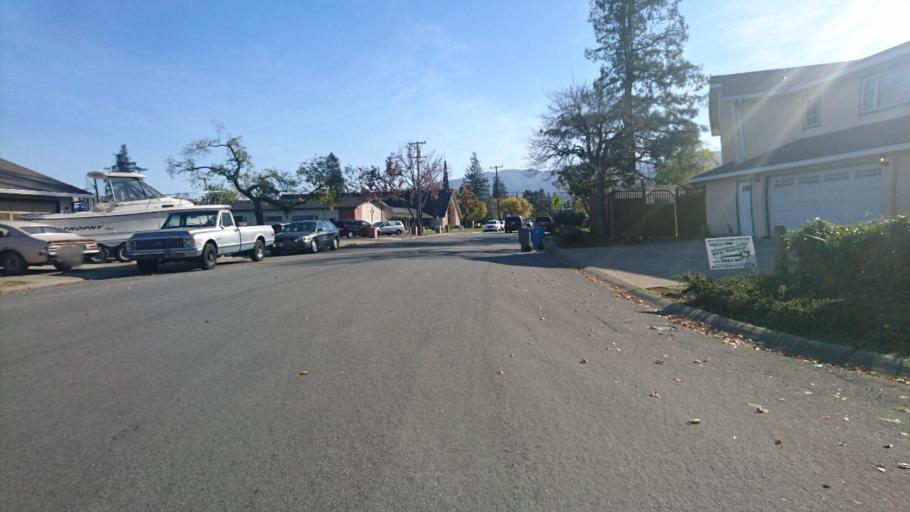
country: US
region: California
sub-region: Santa Clara County
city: Cambrian Park
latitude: 37.2562
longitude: -121.9237
